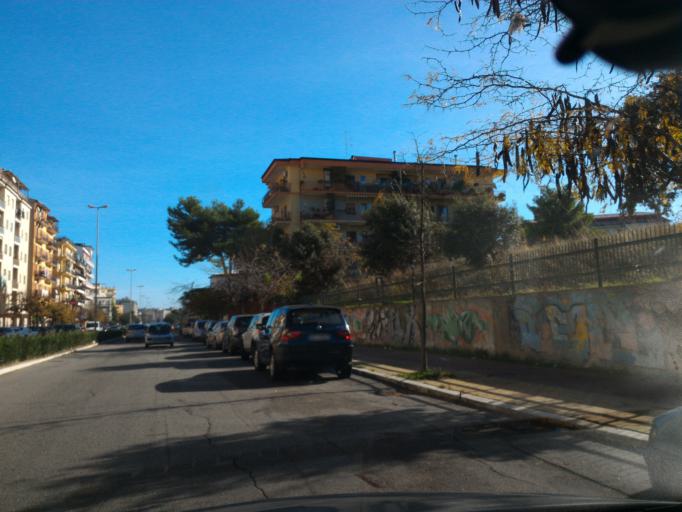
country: IT
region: Calabria
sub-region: Provincia di Crotone
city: Crotone
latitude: 39.0801
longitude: 17.1111
